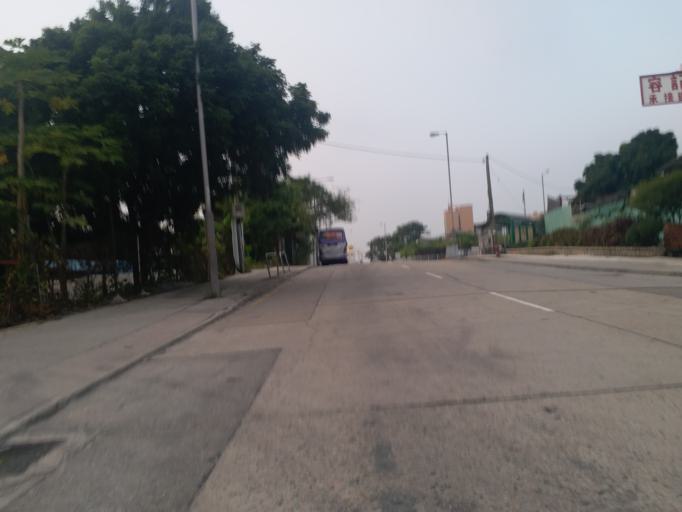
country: HK
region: Yuen Long
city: Yuen Long Kau Hui
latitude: 22.4381
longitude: 114.0113
